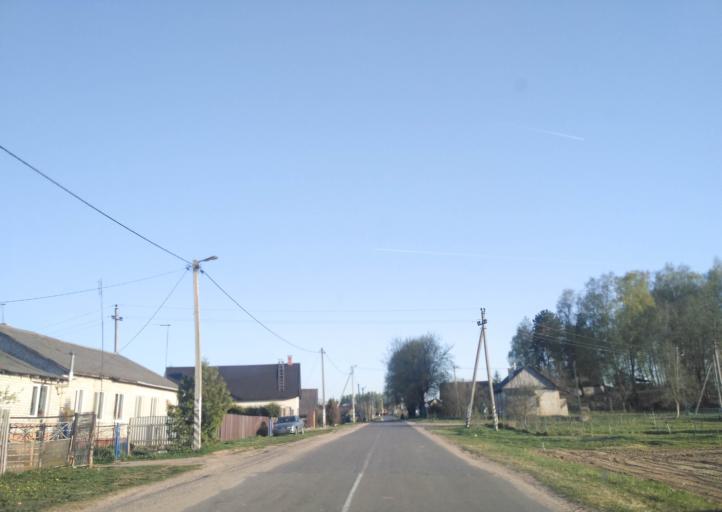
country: BY
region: Minsk
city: Pyatryshki
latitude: 54.1068
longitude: 27.1920
